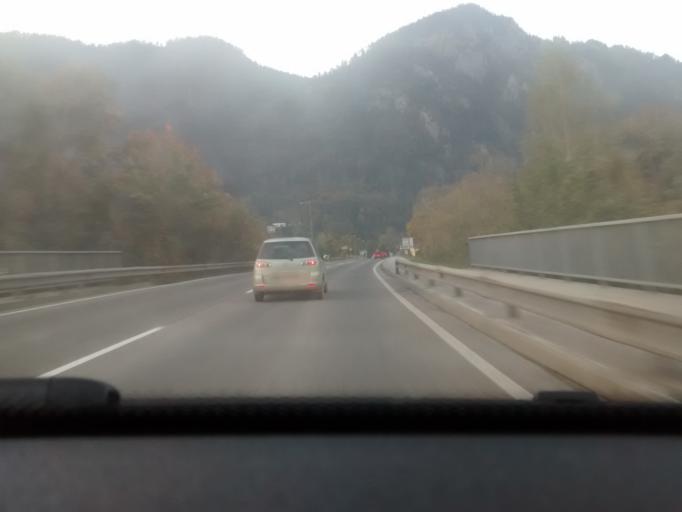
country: AT
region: Upper Austria
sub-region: Politischer Bezirk Gmunden
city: Ebensee
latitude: 47.8093
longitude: 13.7769
